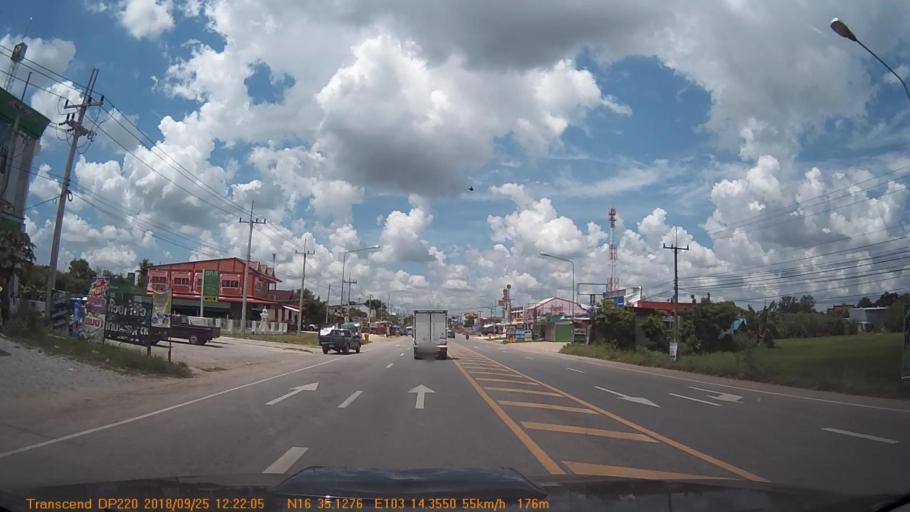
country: TH
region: Kalasin
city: Huai Mek
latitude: 16.5854
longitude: 103.2393
